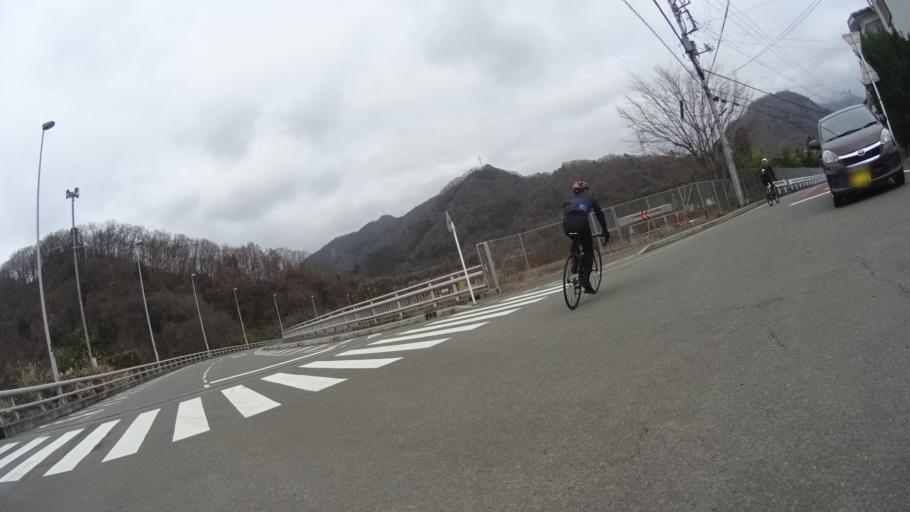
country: JP
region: Yamanashi
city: Otsuki
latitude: 35.6113
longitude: 138.9376
